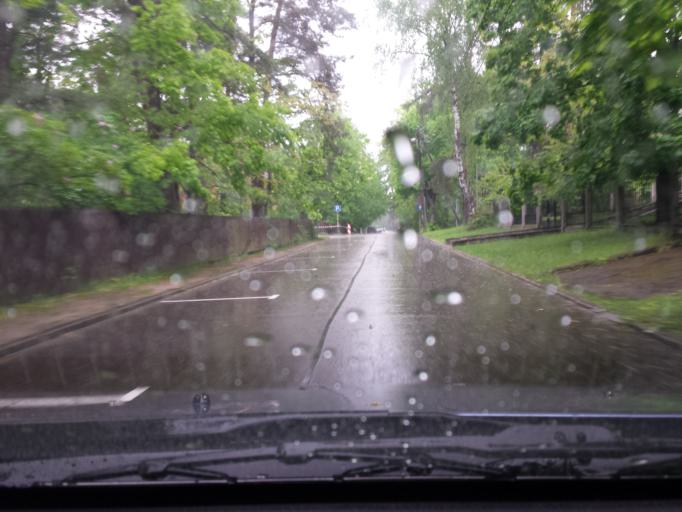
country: LV
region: Riga
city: Jaunciems
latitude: 57.0763
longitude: 24.1128
